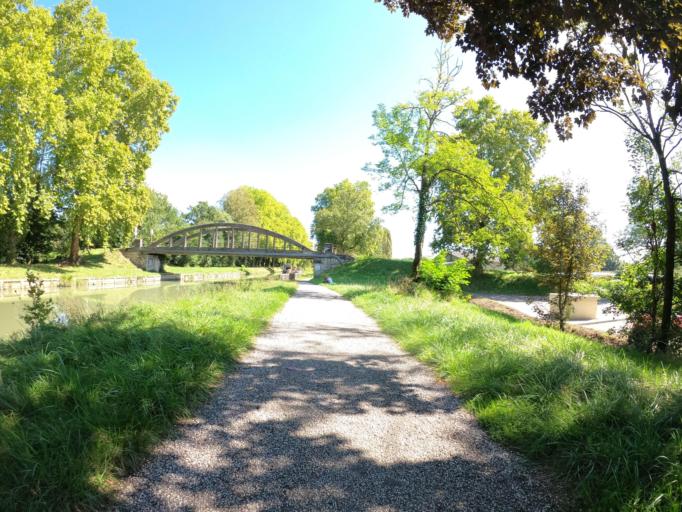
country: FR
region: Midi-Pyrenees
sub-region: Departement du Tarn-et-Garonne
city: Valence
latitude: 44.1158
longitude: 0.8641
